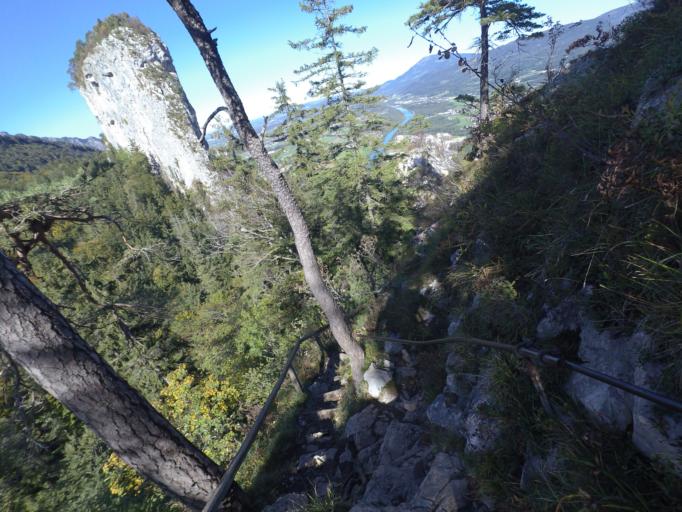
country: AT
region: Salzburg
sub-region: Politischer Bezirk Hallein
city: Hallein
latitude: 47.6891
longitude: 13.0773
